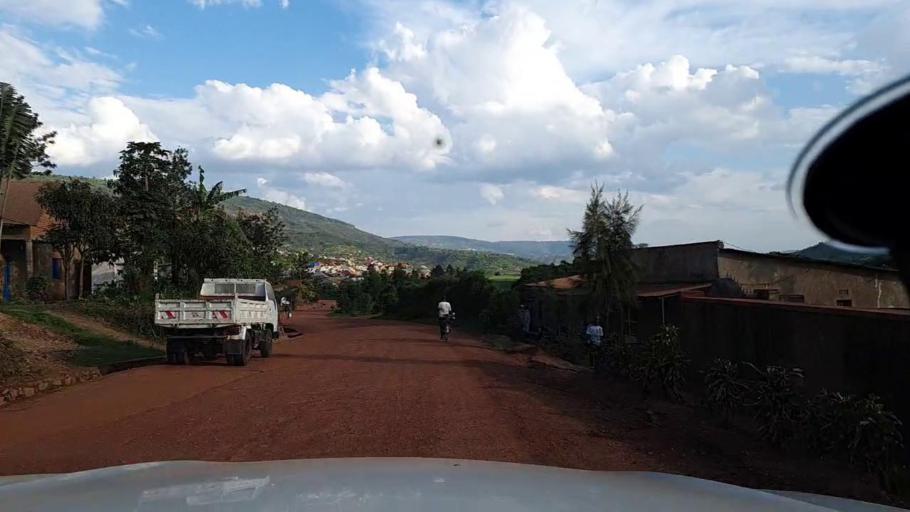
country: RW
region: Kigali
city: Kigali
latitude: -1.9043
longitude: 29.9766
